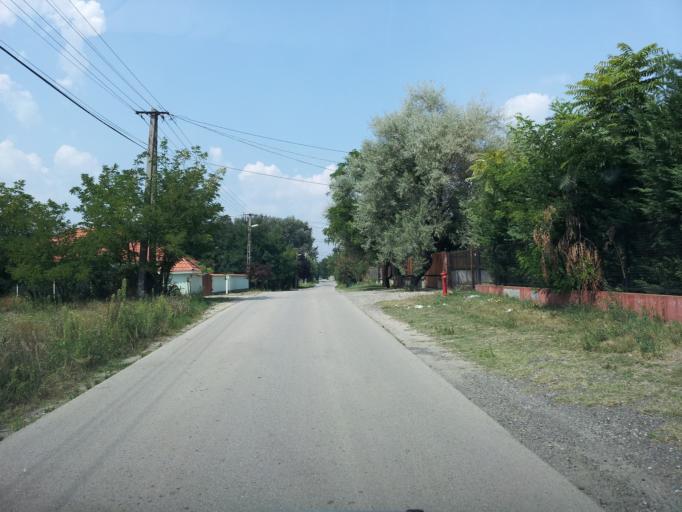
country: HU
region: Pest
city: Szigethalom
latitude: 47.3157
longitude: 19.0203
